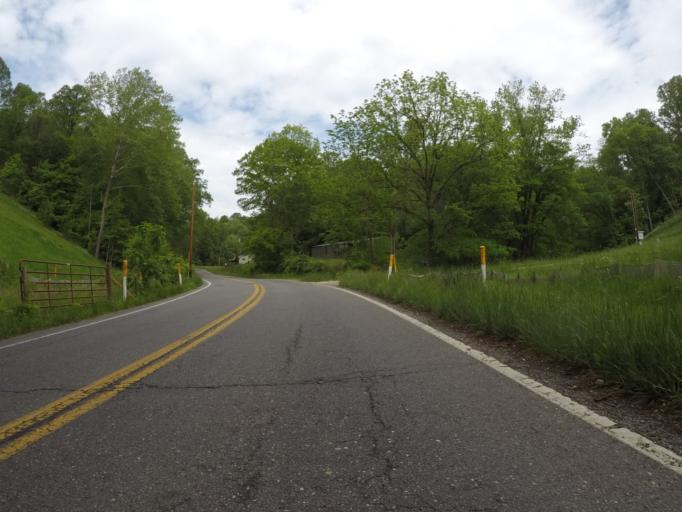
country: US
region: West Virginia
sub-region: Wayne County
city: Ceredo
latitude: 38.3547
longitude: -82.5476
